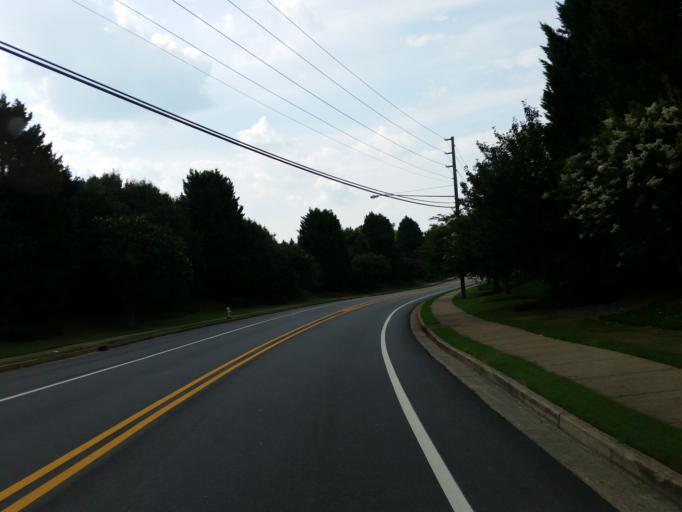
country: US
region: Georgia
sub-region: Fulton County
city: Roswell
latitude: 34.0515
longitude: -84.3817
